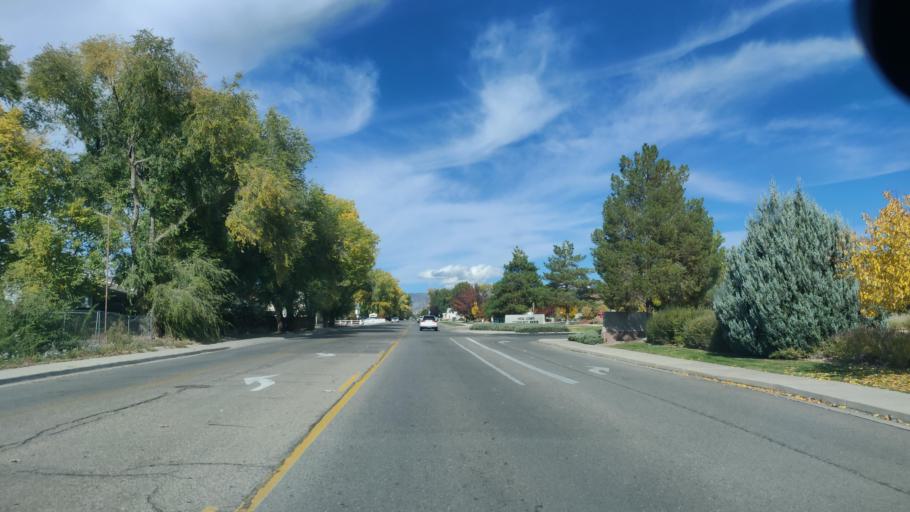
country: US
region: Colorado
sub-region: Mesa County
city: Fruitvale
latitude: 39.0781
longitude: -108.5058
